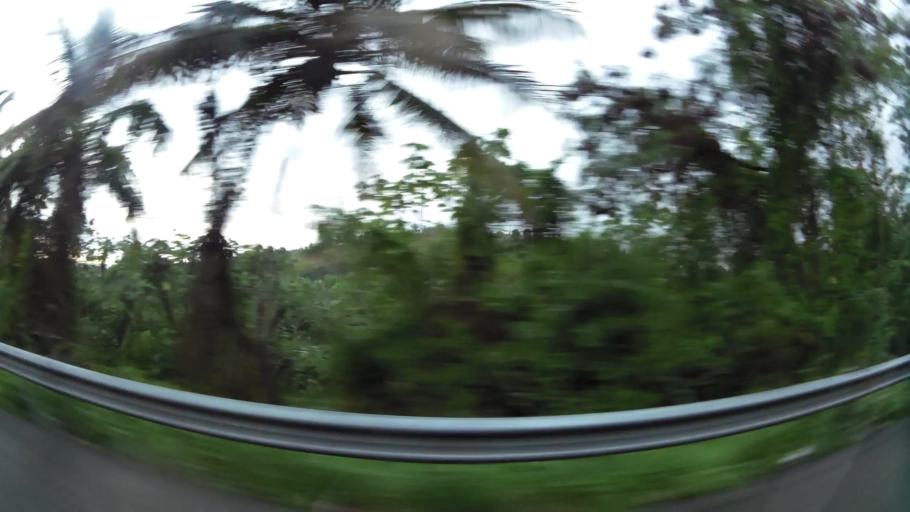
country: DO
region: San Cristobal
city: Villa Altagracia
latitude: 18.6047
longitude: -70.1372
